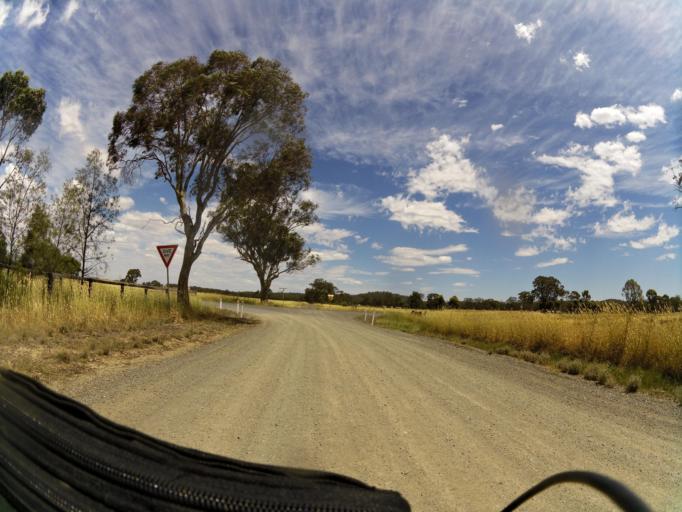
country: AU
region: Victoria
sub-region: Campaspe
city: Kyabram
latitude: -36.7584
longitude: 145.1021
